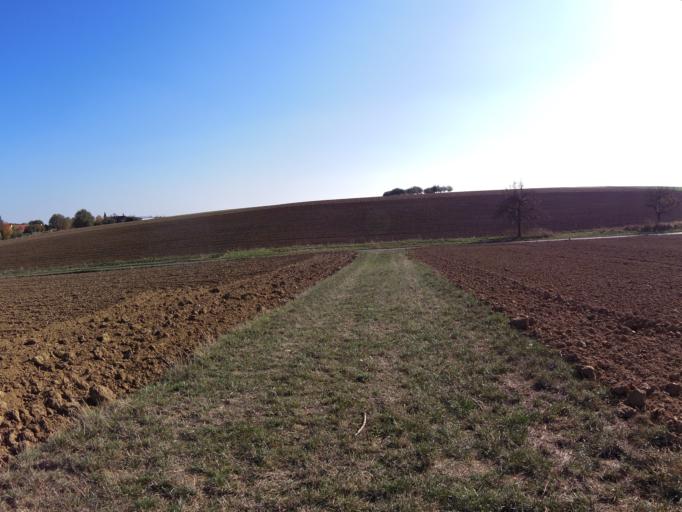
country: DE
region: Bavaria
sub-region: Regierungsbezirk Unterfranken
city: Geroldshausen
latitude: 49.6940
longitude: 9.9223
